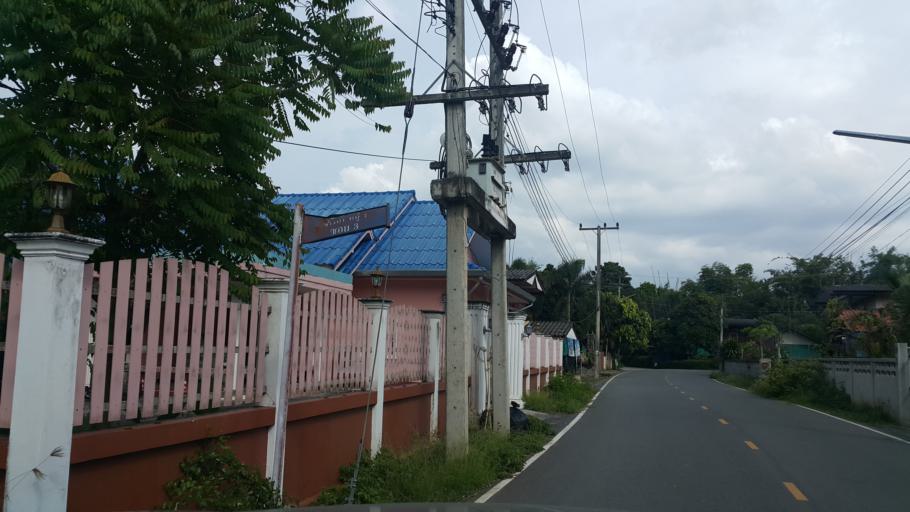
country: TH
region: Chiang Mai
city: San Sai
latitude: 18.9068
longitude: 99.1280
